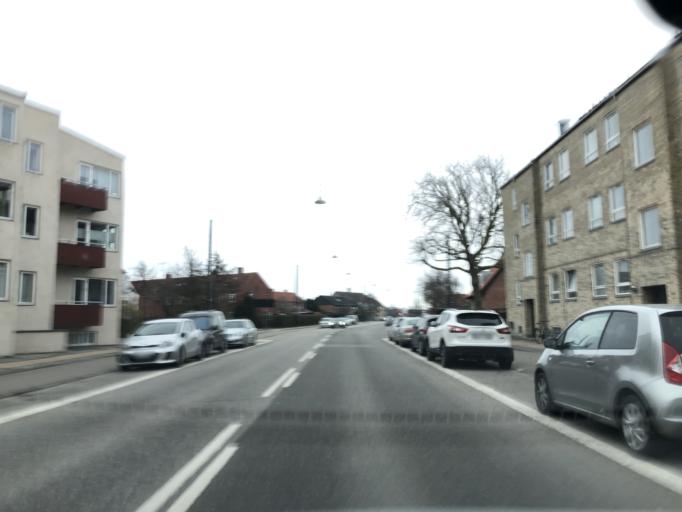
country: DK
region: Capital Region
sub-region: Tarnby Kommune
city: Tarnby
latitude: 55.6460
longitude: 12.6257
